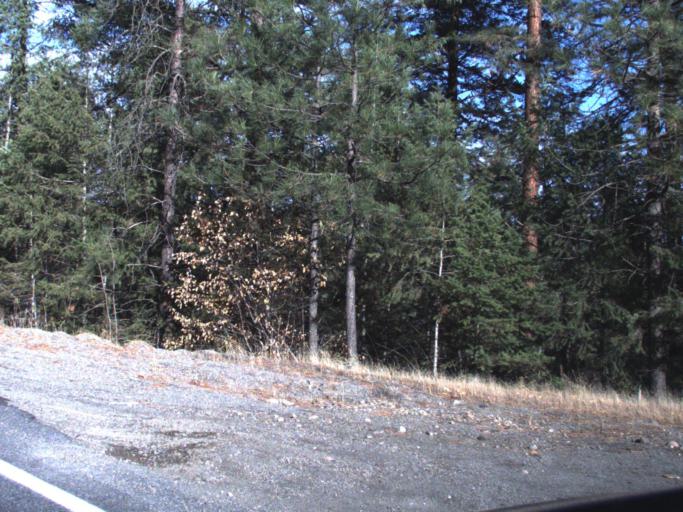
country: US
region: Washington
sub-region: Stevens County
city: Kettle Falls
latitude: 48.5749
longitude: -118.0839
